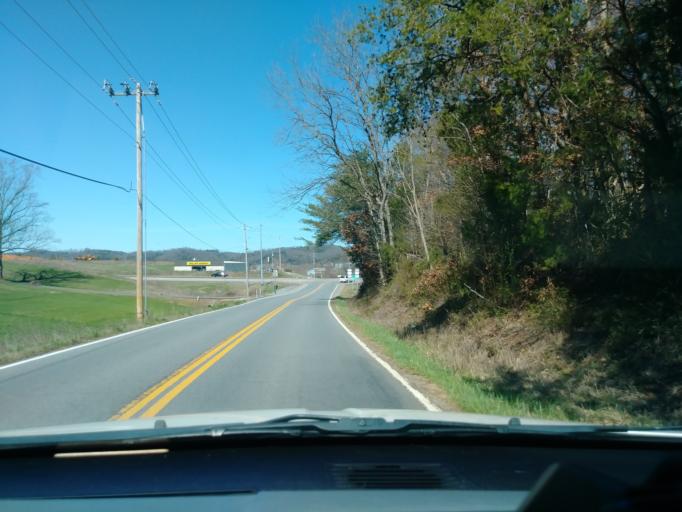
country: US
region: Tennessee
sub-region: Cocke County
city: Newport
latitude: 36.0031
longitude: -83.0898
